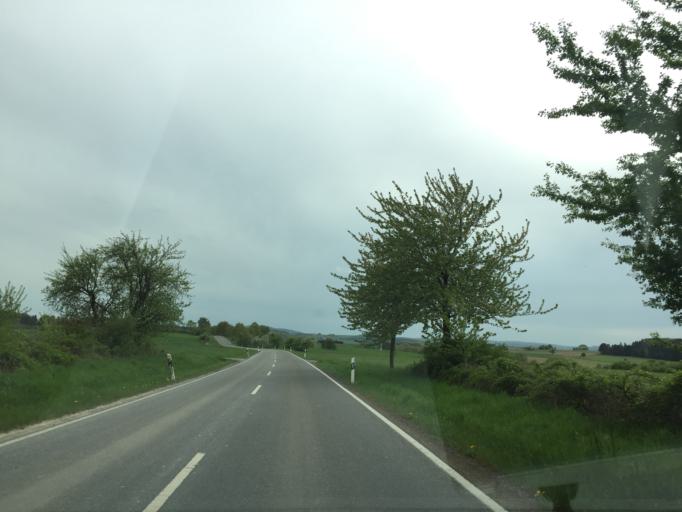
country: DE
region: Rheinland-Pfalz
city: Berod bei Wallmerod
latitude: 50.4772
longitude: 7.9351
